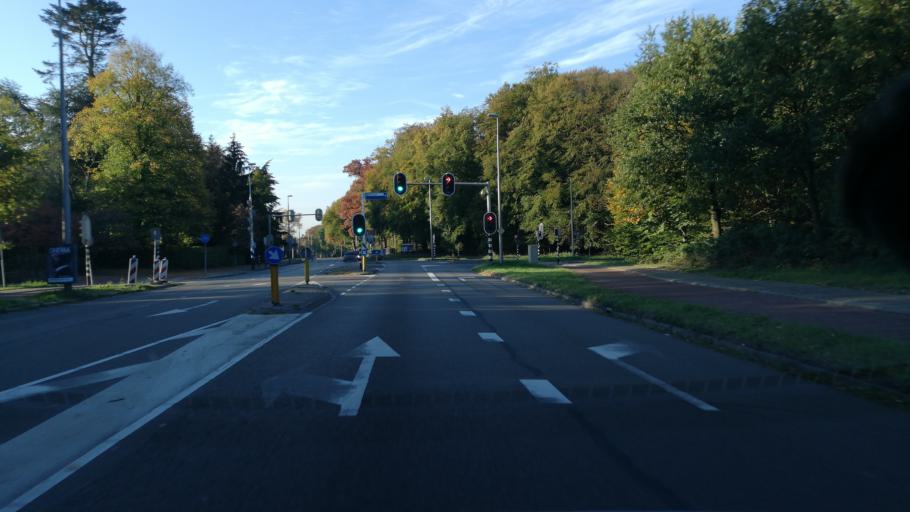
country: NL
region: Gelderland
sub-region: Gemeente Arnhem
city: Arnhem
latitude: 51.9952
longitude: 5.9111
